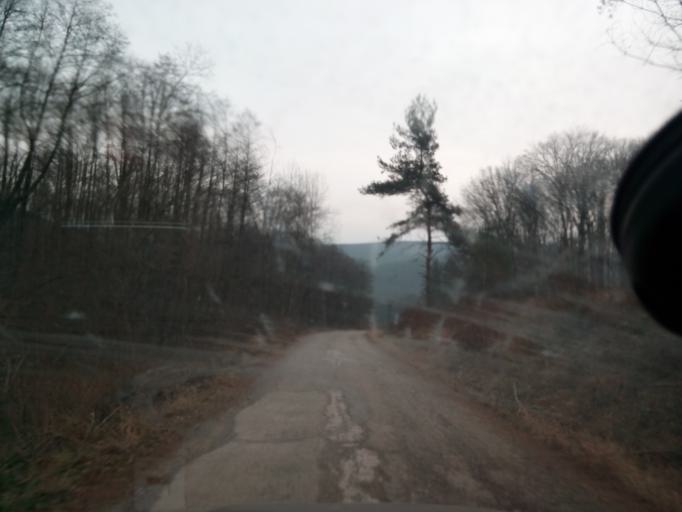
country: SK
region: Kosicky
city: Medzev
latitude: 48.6832
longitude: 20.8928
